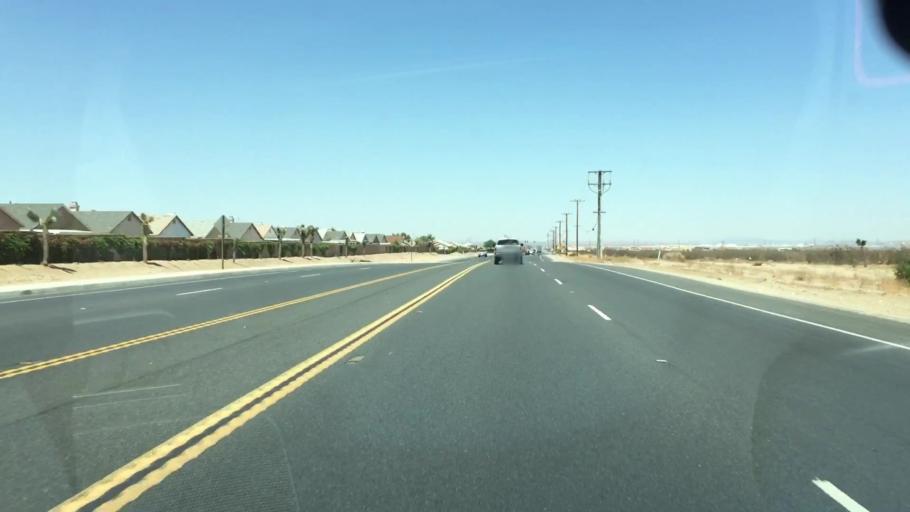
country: US
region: California
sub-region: San Bernardino County
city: Mountain View Acres
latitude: 34.4943
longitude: -117.3995
